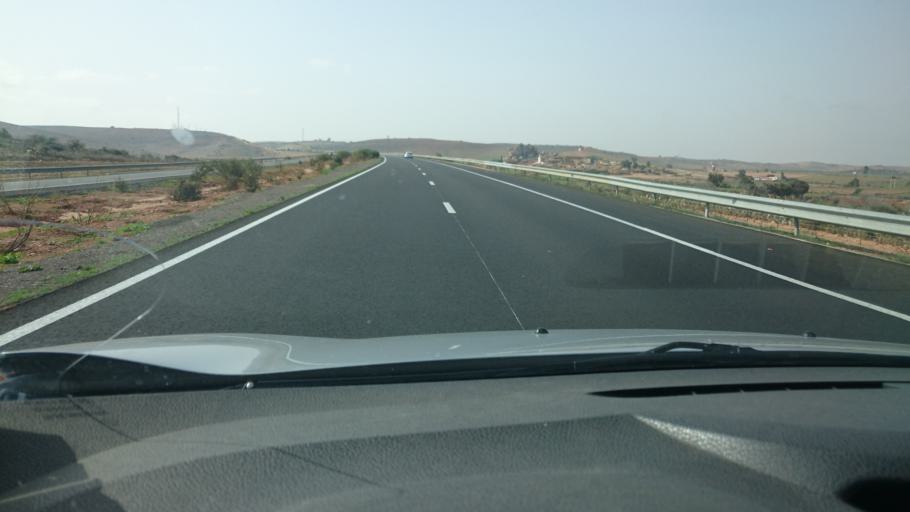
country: MA
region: Marrakech-Tensift-Al Haouz
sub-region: Kelaa-Des-Sraghna
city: Sidi Abdallah
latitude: 32.5454
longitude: -7.8994
